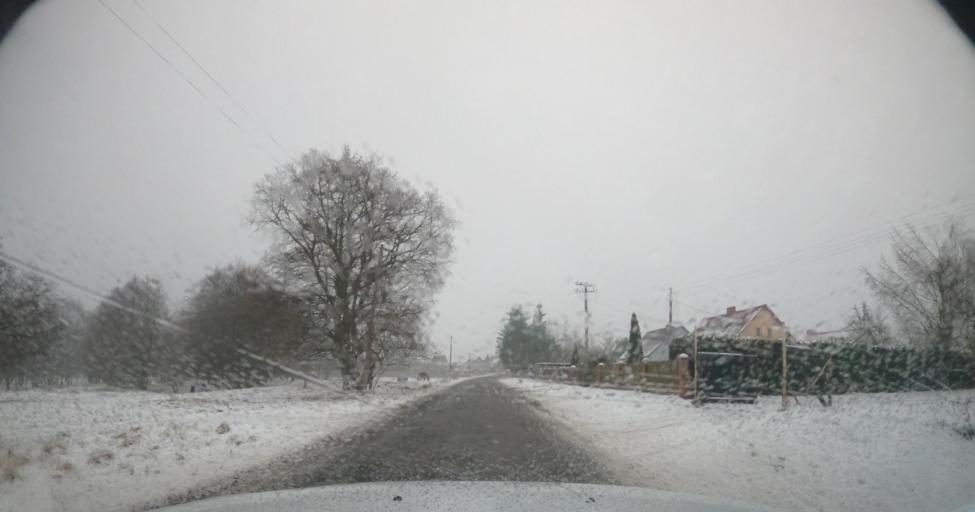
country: PL
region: West Pomeranian Voivodeship
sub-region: Powiat goleniowski
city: Przybiernow
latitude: 53.6917
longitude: 14.8615
